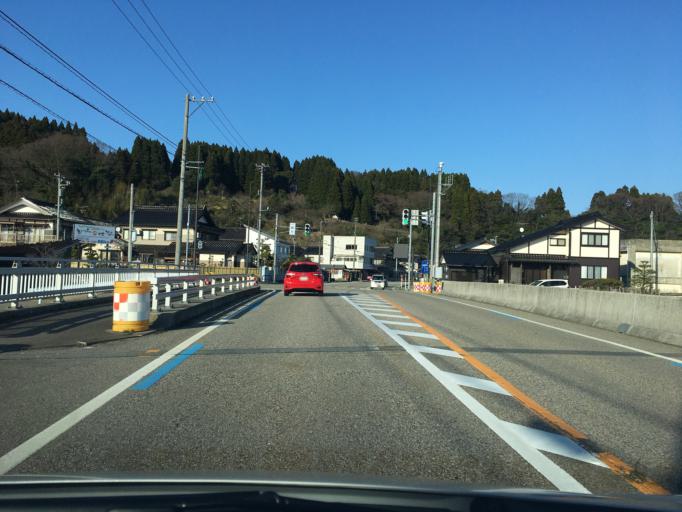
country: JP
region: Toyama
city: Himi
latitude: 36.9122
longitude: 137.0190
